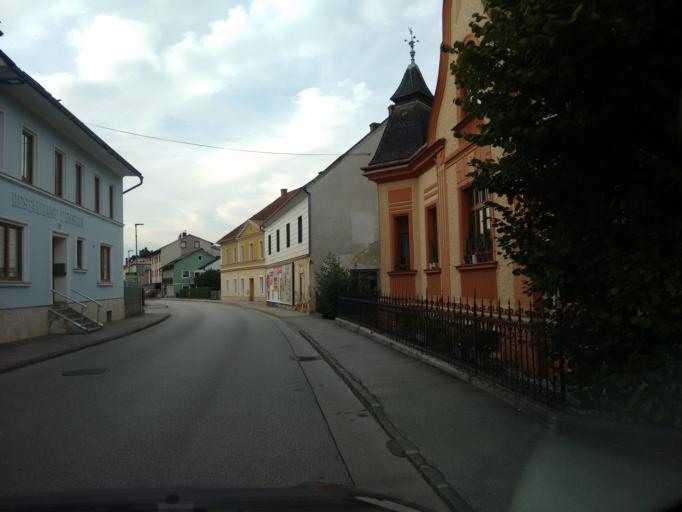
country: AT
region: Upper Austria
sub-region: Politischer Bezirk Steyr-Land
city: Bad Hall
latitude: 48.0320
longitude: 14.2142
